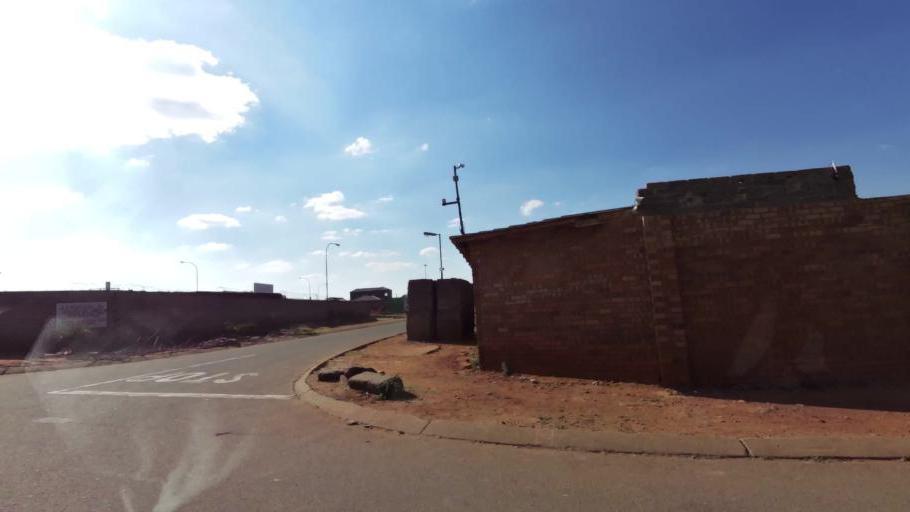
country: ZA
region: Gauteng
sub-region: City of Johannesburg Metropolitan Municipality
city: Soweto
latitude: -26.2317
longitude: 27.8777
